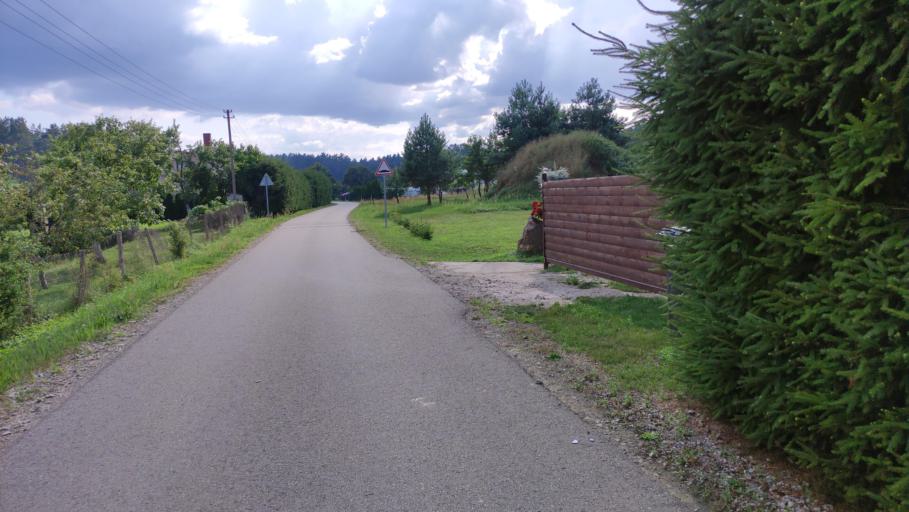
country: LT
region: Alytaus apskritis
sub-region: Alytus
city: Alytus
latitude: 54.4305
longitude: 24.0656
